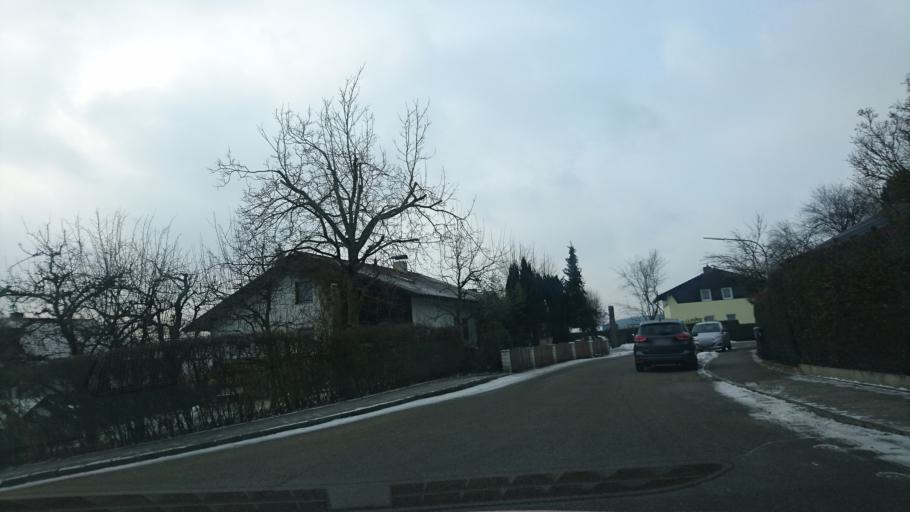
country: DE
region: Bavaria
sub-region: Lower Bavaria
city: Bad Griesbach
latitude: 48.4403
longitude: 13.1934
